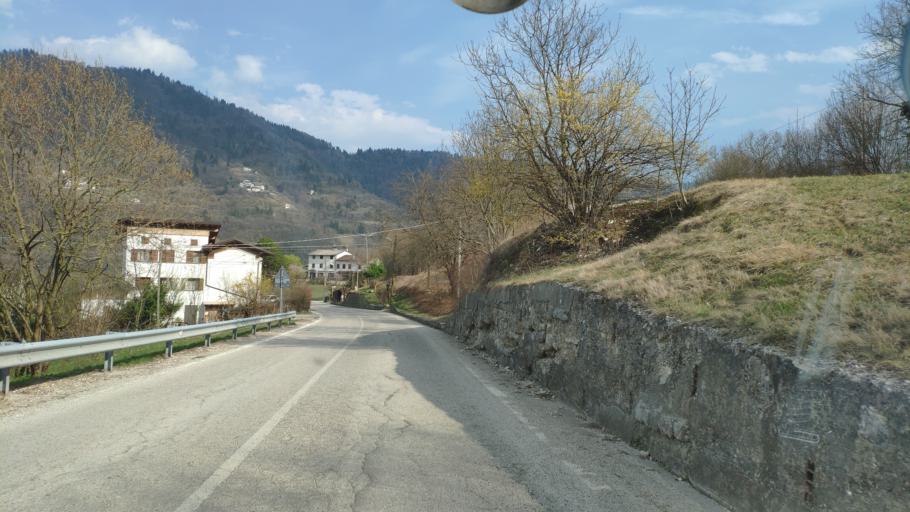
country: IT
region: Veneto
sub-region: Provincia di Vicenza
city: Enego
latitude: 45.9504
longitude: 11.7151
